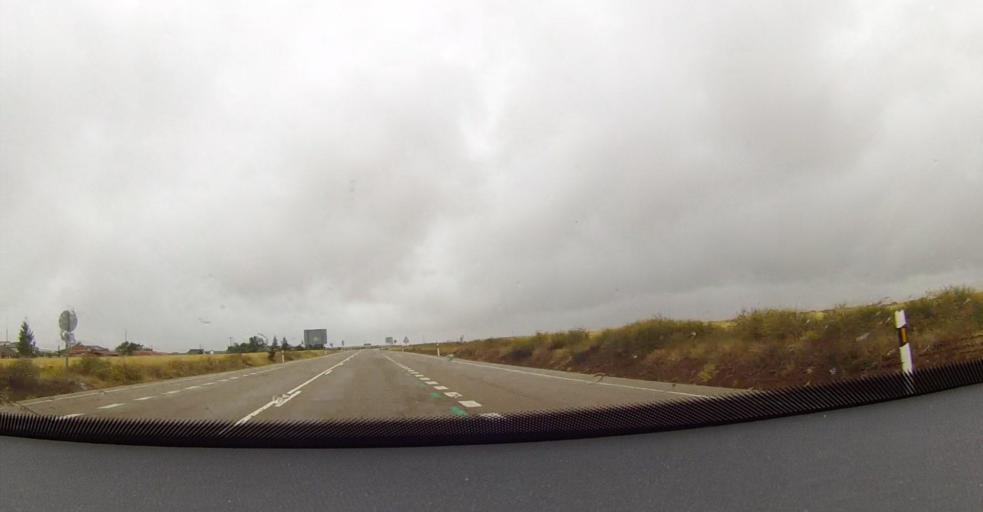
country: ES
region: Castille and Leon
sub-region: Provincia de Palencia
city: Poza de la Vega
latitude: 42.5705
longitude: -4.7567
